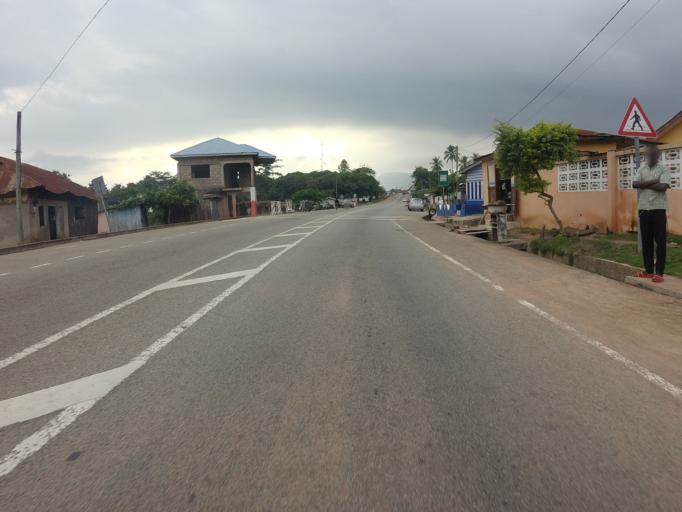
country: GH
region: Volta
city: Ho
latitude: 6.7709
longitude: 0.4807
